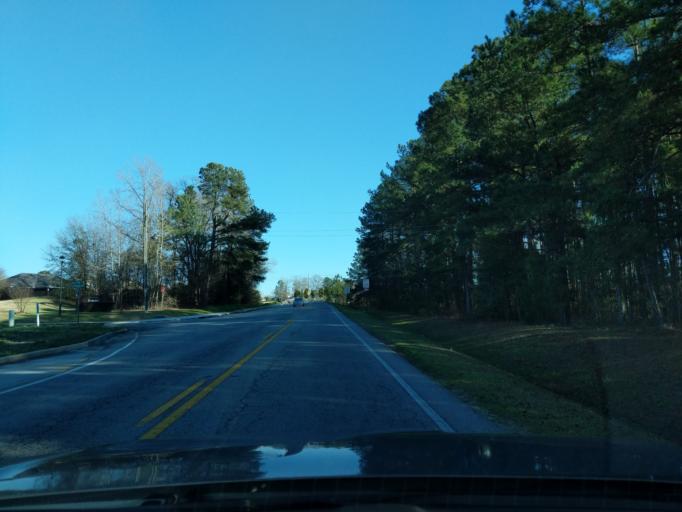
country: US
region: Georgia
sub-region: Columbia County
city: Grovetown
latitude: 33.4535
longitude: -82.2255
